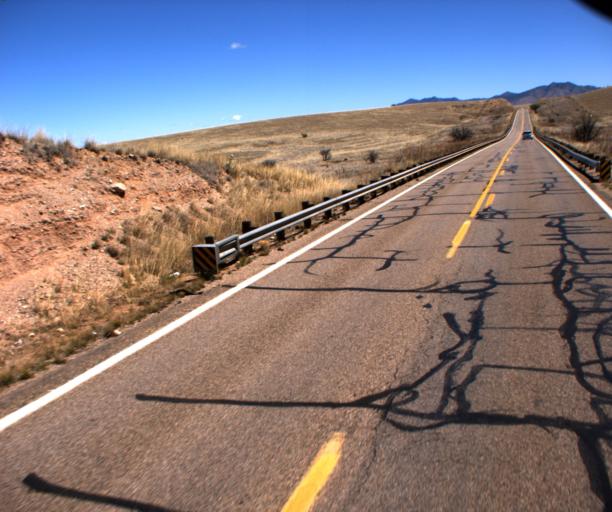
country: US
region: Arizona
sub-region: Cochise County
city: Huachuca City
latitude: 31.7033
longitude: -110.5870
